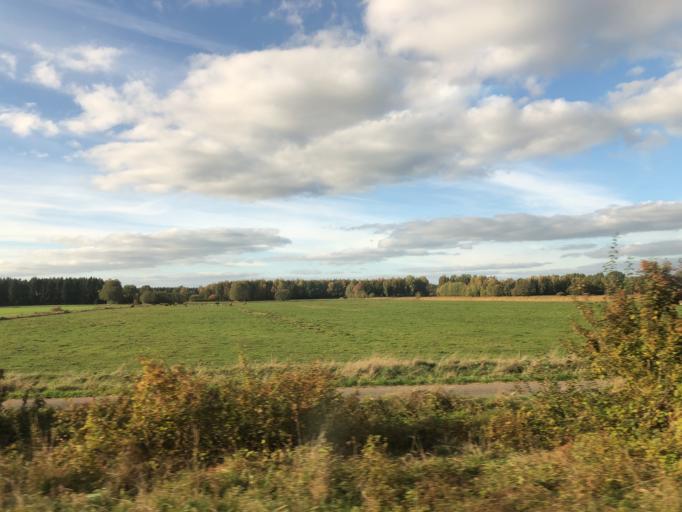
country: DE
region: Schleswig-Holstein
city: Borstel
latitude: 53.9757
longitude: 9.7960
